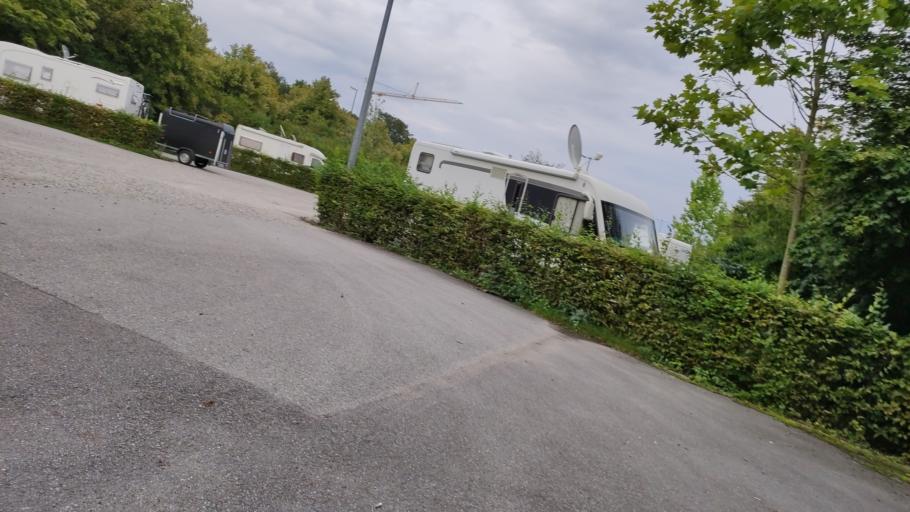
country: DE
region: Bavaria
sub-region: Swabia
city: Konigsbrunn
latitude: 48.2724
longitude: 10.8820
